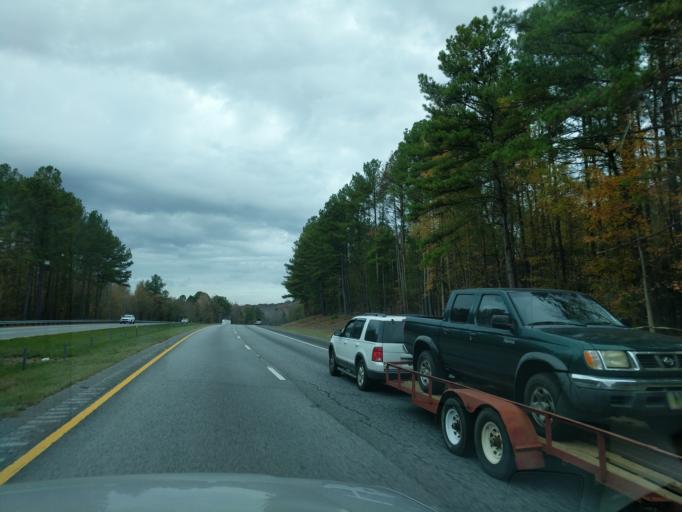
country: US
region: South Carolina
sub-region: Spartanburg County
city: Woodruff
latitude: 34.6759
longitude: -81.9361
